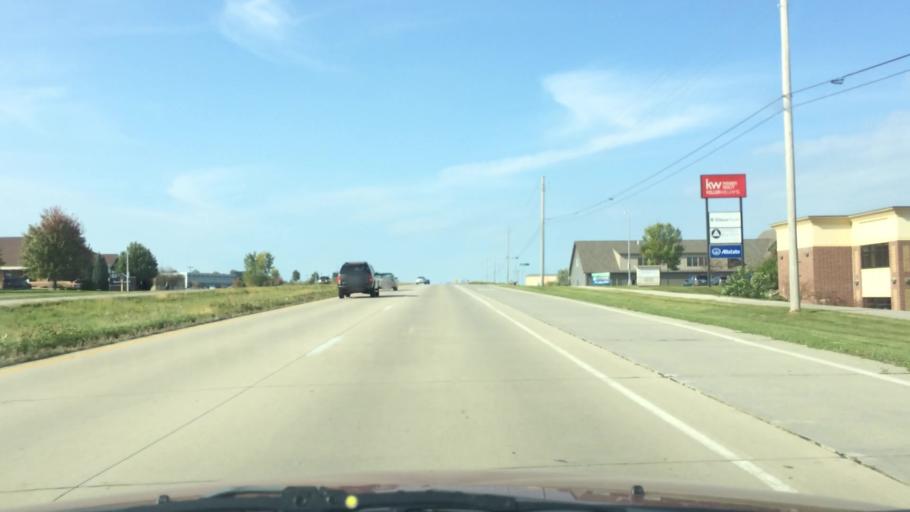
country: US
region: Minnesota
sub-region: Olmsted County
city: Rochester
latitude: 44.0524
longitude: -92.5226
